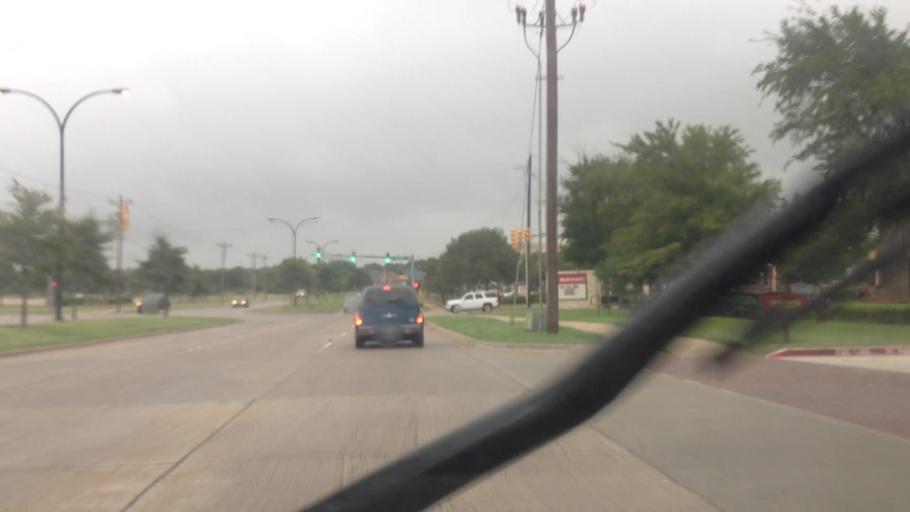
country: US
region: Texas
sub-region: Tarrant County
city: Keller
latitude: 32.8982
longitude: -97.2385
